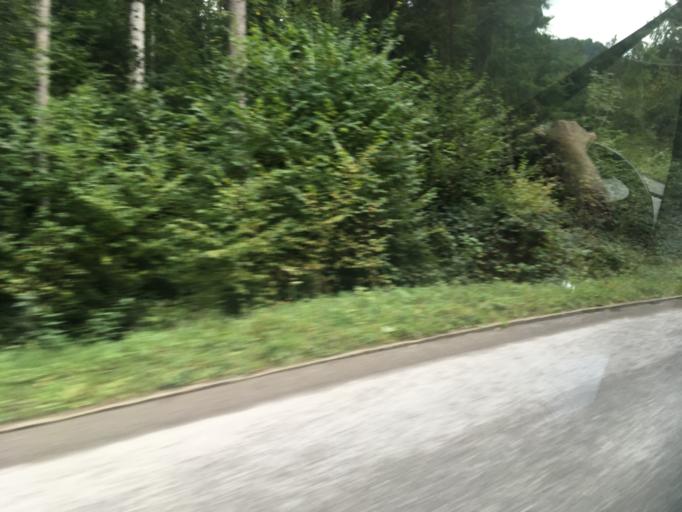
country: CH
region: Fribourg
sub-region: Sense District
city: Oberschrot
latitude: 46.7215
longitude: 7.2462
